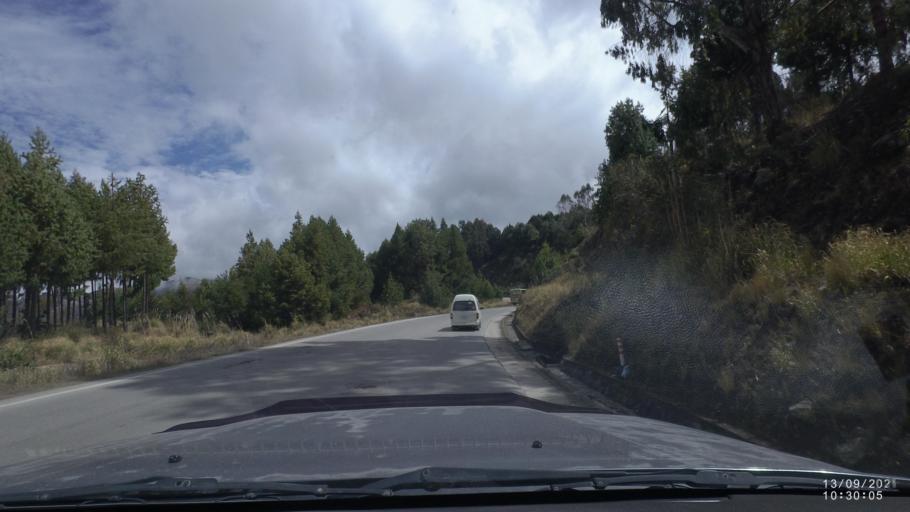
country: BO
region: Cochabamba
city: Colomi
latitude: -17.2650
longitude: -65.8850
